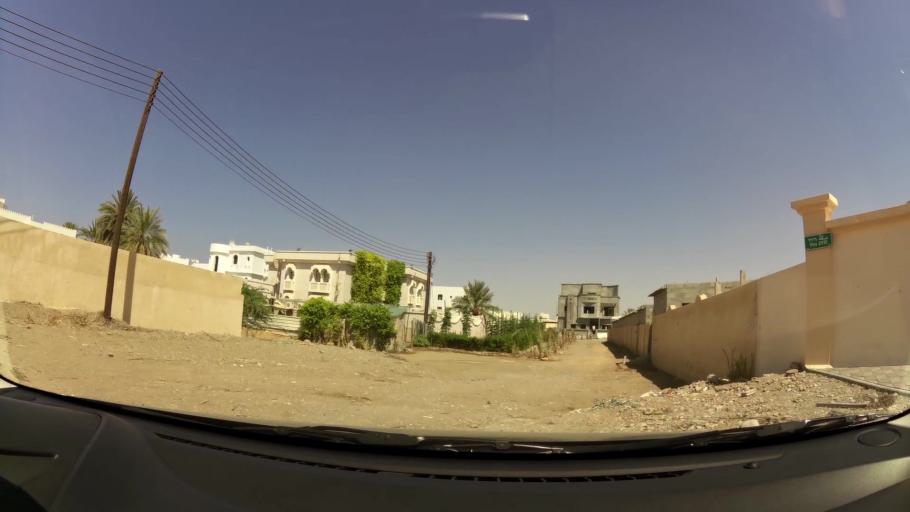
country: OM
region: Muhafazat Masqat
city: As Sib al Jadidah
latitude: 23.6312
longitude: 58.2197
